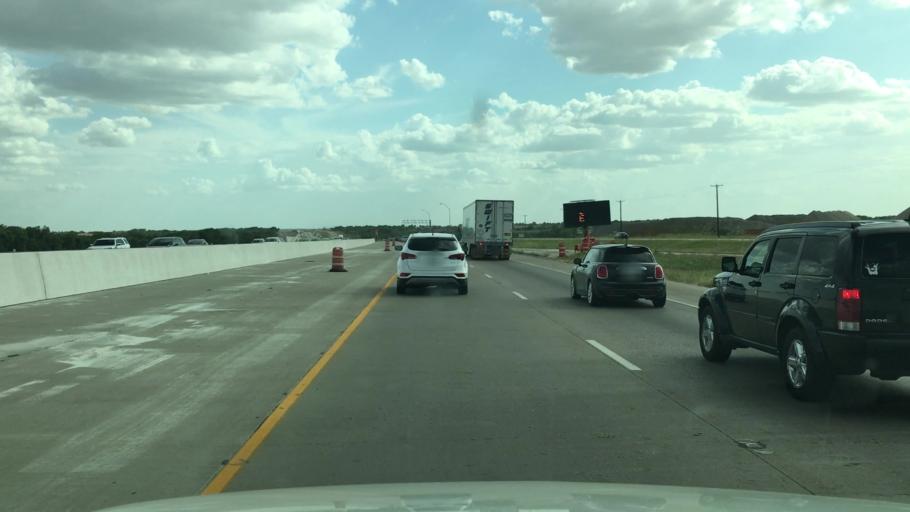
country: US
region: Texas
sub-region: McLennan County
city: Bruceville-Eddy
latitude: 31.2752
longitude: -97.2637
